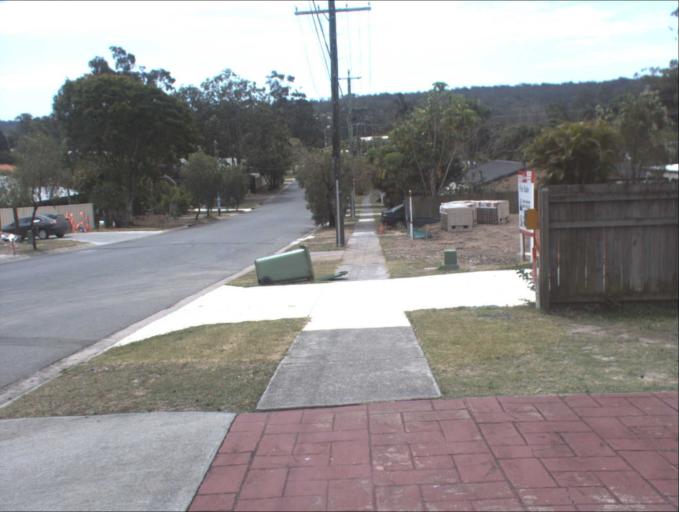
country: AU
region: Queensland
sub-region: Logan
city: Slacks Creek
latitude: -27.6489
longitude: 153.1656
